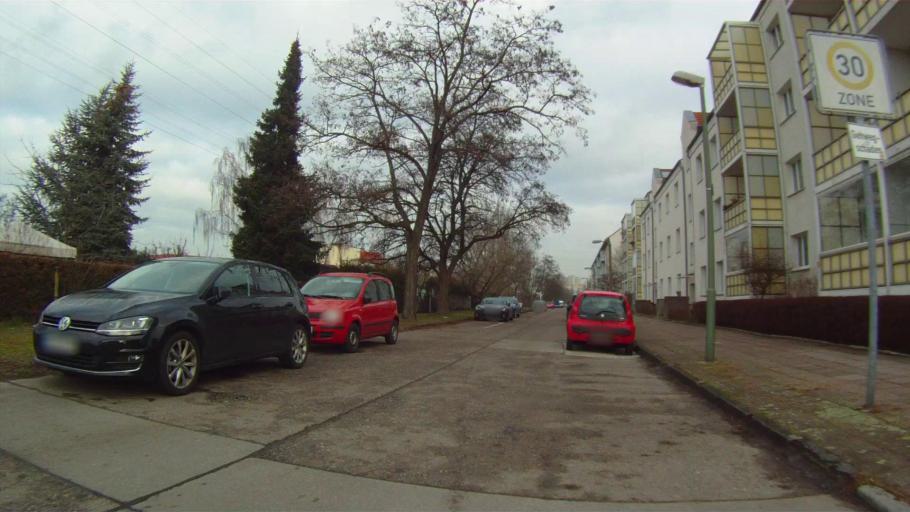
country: DE
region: Berlin
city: Karlshorst
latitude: 52.4874
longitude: 13.5158
